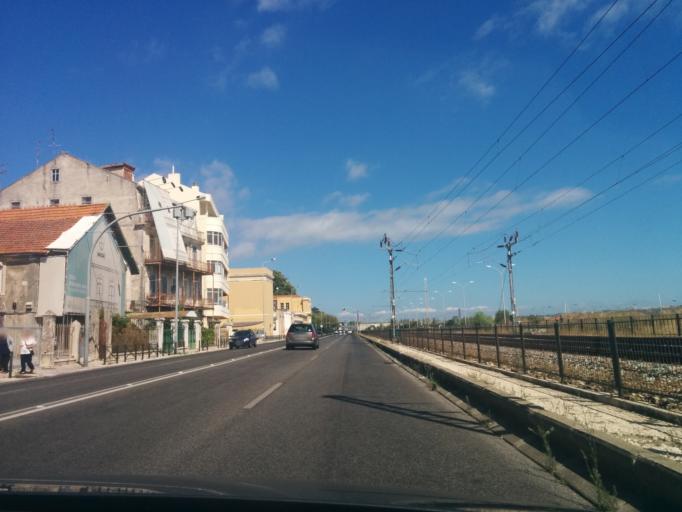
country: PT
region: Lisbon
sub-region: Oeiras
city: Alges
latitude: 38.6991
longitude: -9.2405
